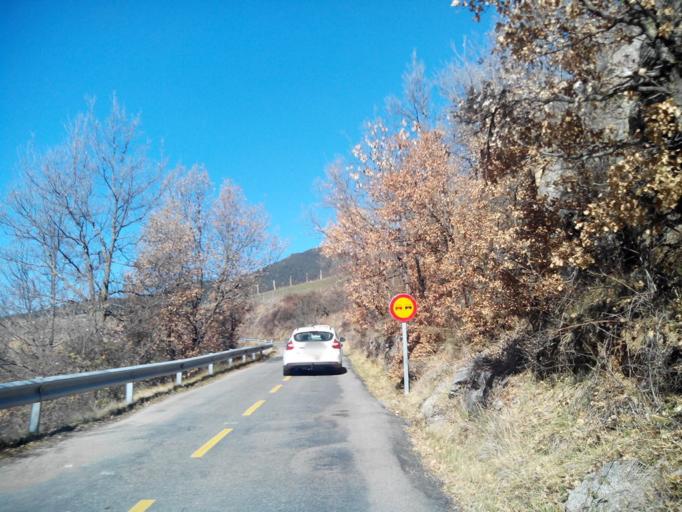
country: ES
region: Catalonia
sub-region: Provincia de Lleida
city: Lles de Cerdanya
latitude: 42.3843
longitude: 1.6817
